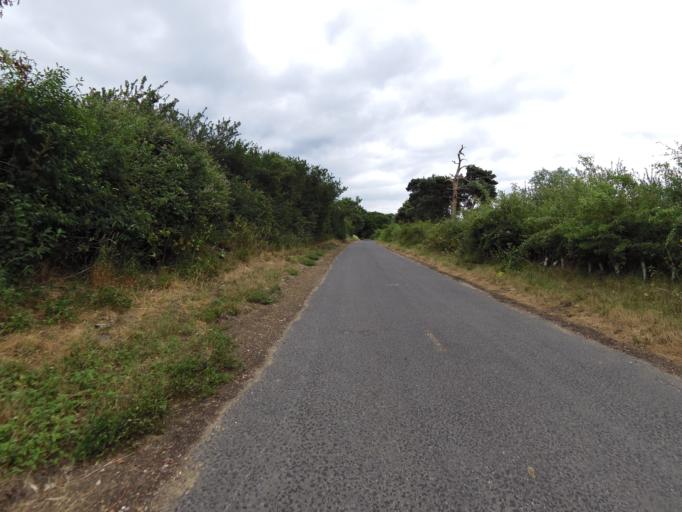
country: GB
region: England
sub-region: Suffolk
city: Bungay
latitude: 52.4391
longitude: 1.3926
